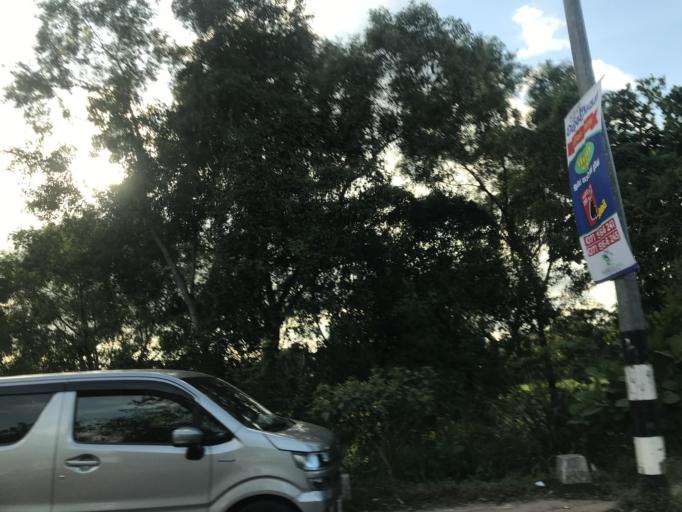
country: LK
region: Western
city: Gampaha
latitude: 7.0990
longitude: 79.9913
